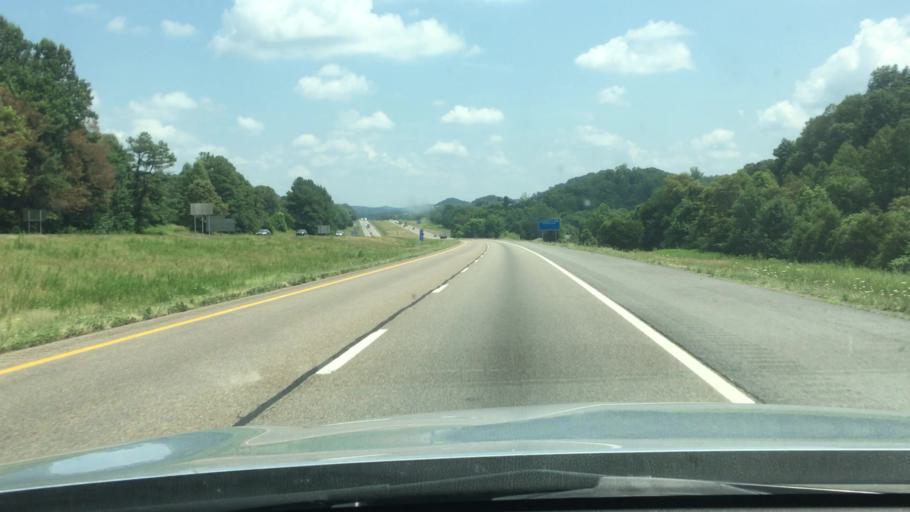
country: US
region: Tennessee
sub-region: Washington County
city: Spurgeon
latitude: 36.5138
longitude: -82.4127
